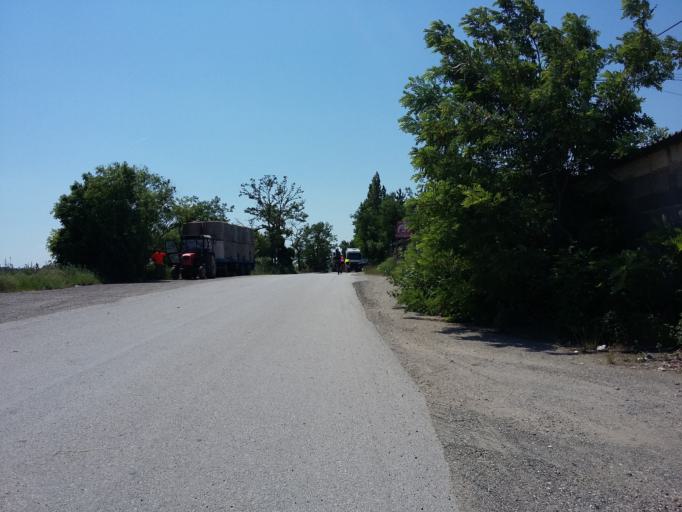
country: AT
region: Lower Austria
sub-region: Politischer Bezirk Ganserndorf
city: Marchegg
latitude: 48.2955
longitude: 16.9681
